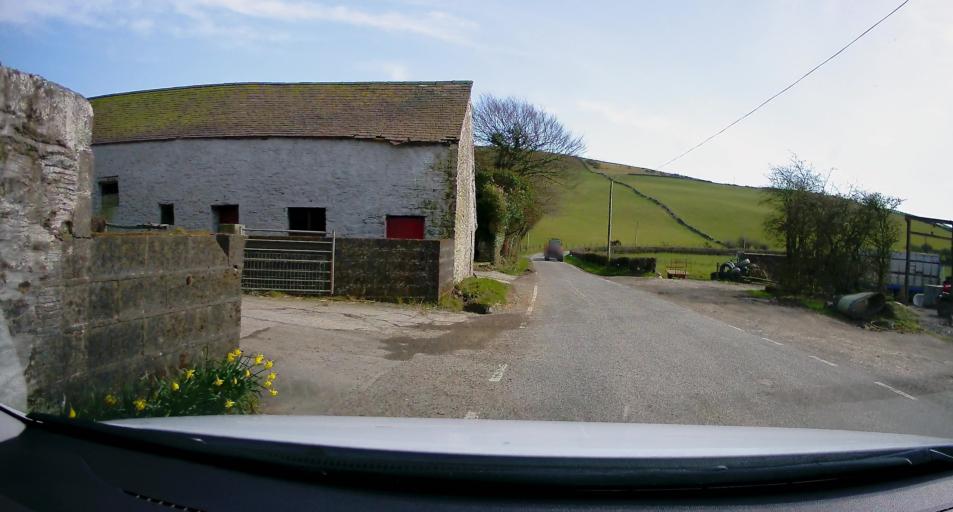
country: GB
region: Wales
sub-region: County of Ceredigion
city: Lledrod
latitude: 52.2703
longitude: -4.0680
